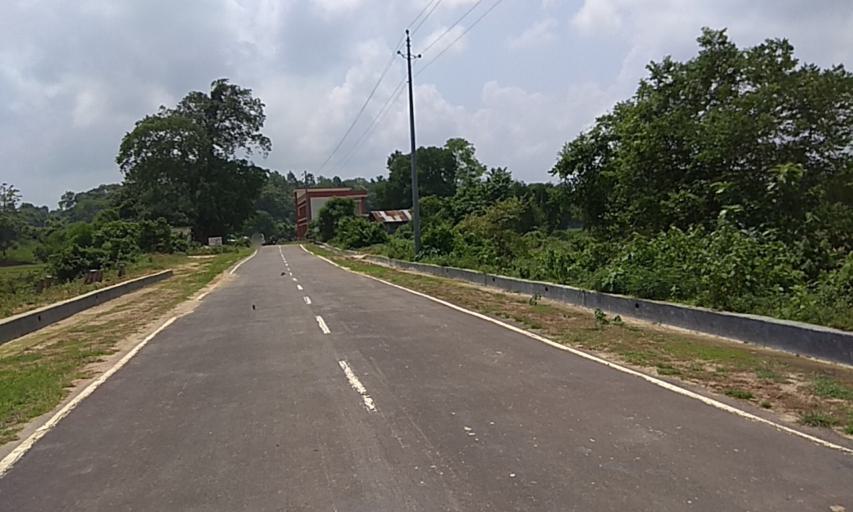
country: BD
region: Chittagong
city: Manikchari
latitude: 22.9357
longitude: 91.9092
